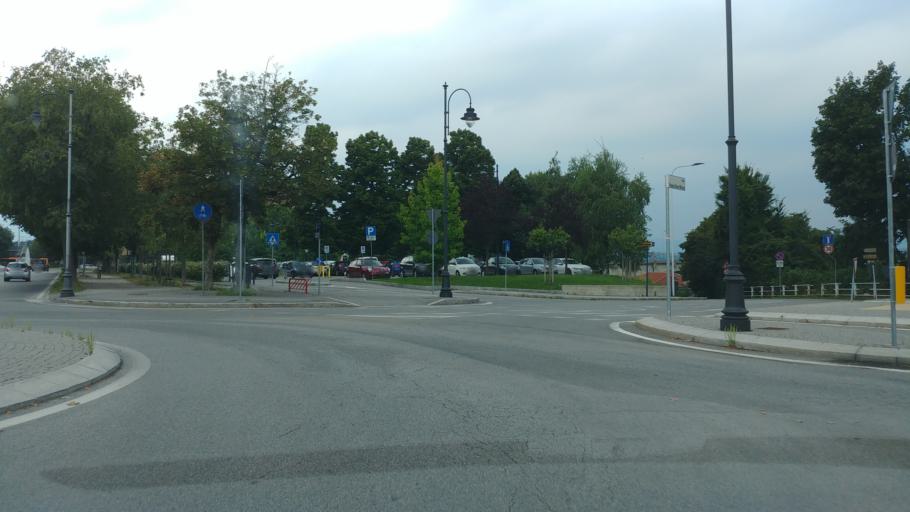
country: IT
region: Piedmont
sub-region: Provincia di Cuneo
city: Cuneo
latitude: 44.3922
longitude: 7.5451
